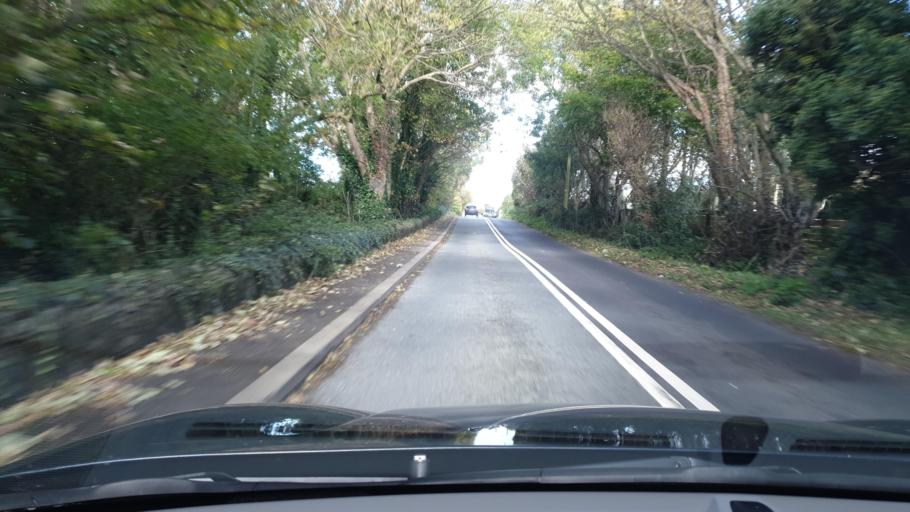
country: IE
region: Leinster
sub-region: Fingal County
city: Skerries
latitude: 53.5641
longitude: -6.1030
